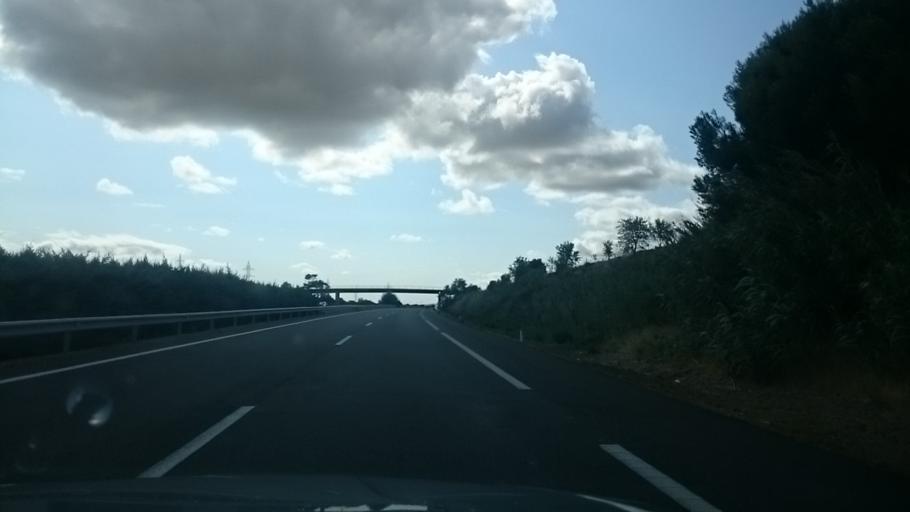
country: ES
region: La Rioja
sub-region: Provincia de La Rioja
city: Calahorra
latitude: 42.2849
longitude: -1.9477
